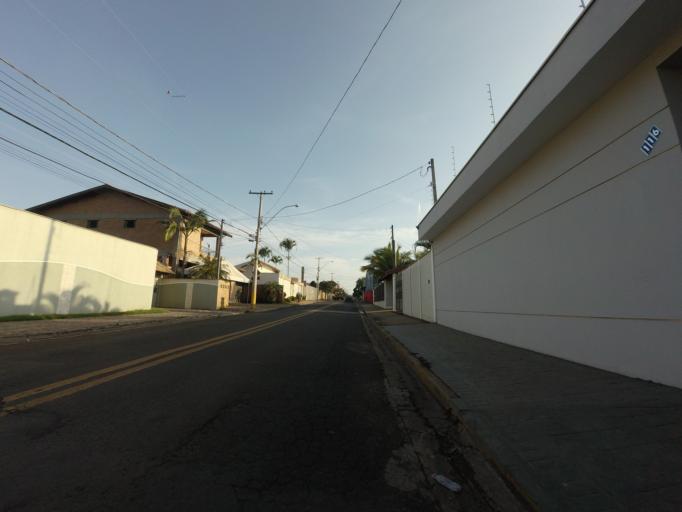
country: BR
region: Sao Paulo
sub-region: Piracicaba
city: Piracicaba
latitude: -22.7405
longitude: -47.6109
